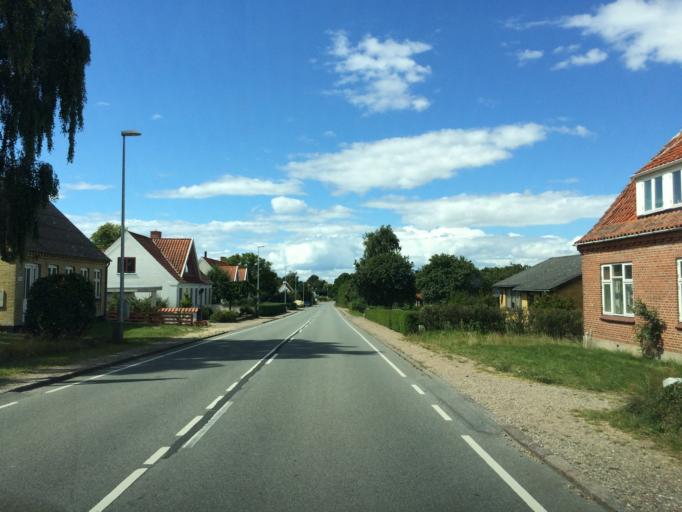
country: DK
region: South Denmark
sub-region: Faaborg-Midtfyn Kommune
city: Faaborg
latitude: 55.1309
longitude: 10.2104
